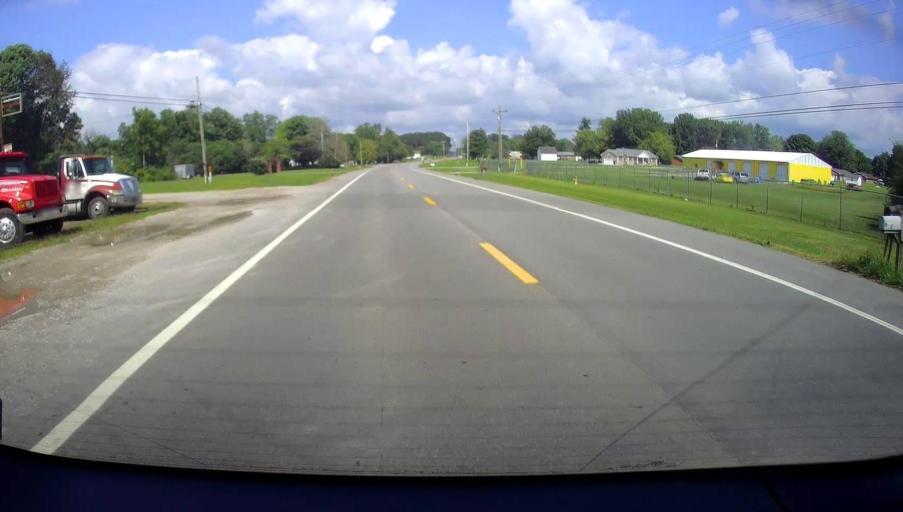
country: US
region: Tennessee
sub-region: Coffee County
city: Manchester
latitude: 35.5021
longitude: -86.1144
